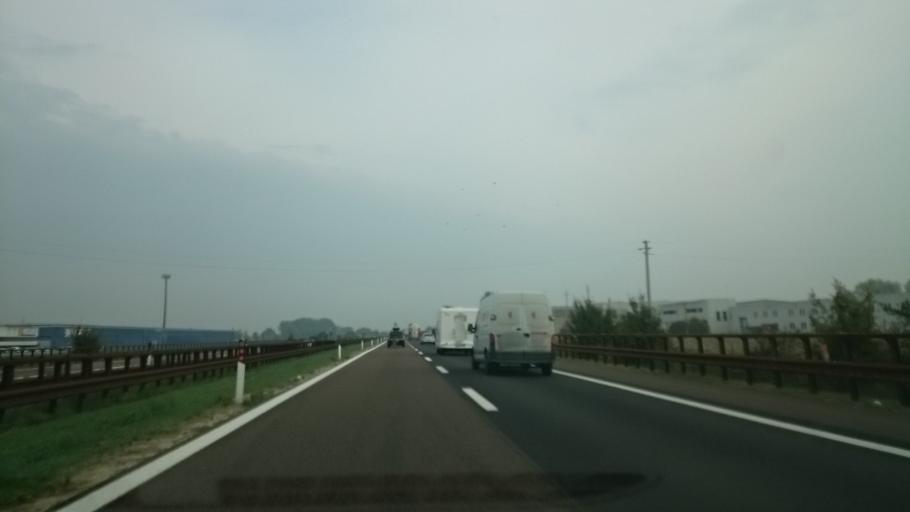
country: IT
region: Lombardy
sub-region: Provincia di Mantova
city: Bondeno
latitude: 44.9326
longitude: 10.8606
